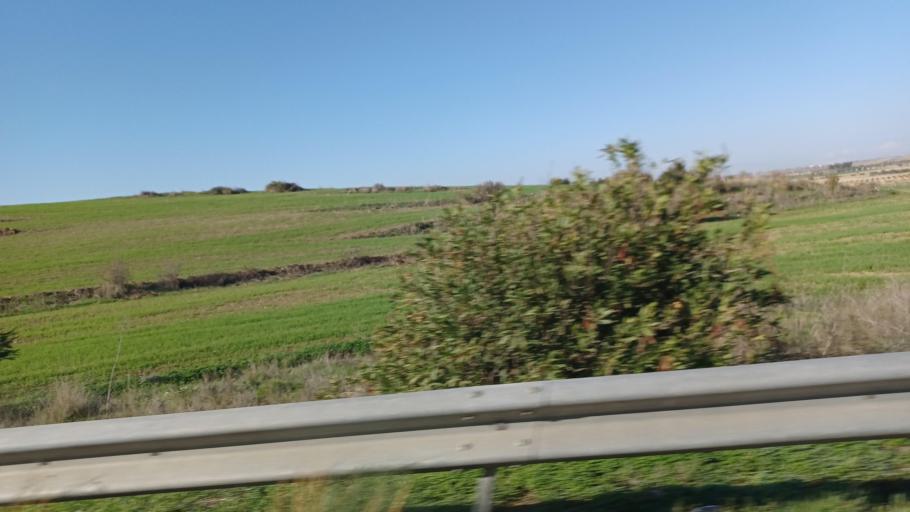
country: CY
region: Lefkosia
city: Lympia
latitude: 35.0218
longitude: 33.4945
